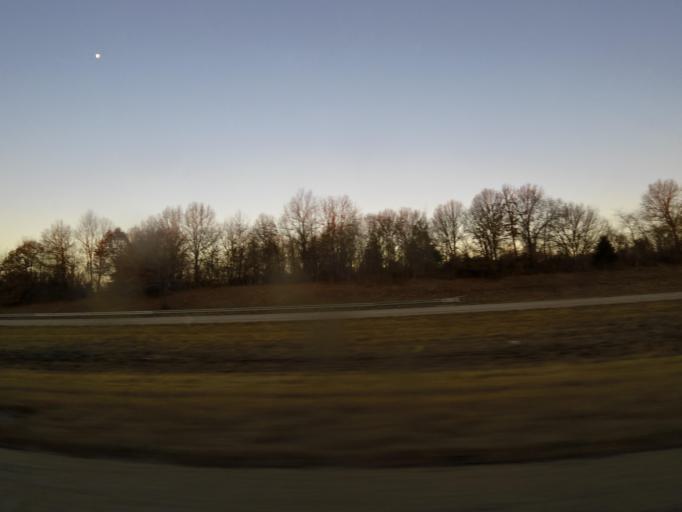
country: US
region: Illinois
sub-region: Marion County
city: Salem
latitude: 38.6928
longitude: -88.9653
